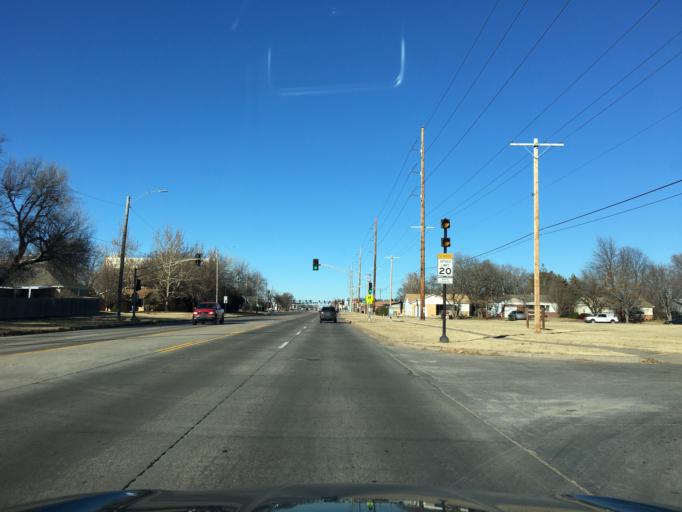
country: US
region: Kansas
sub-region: Sedgwick County
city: Bellaire
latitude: 37.6745
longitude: -97.2444
